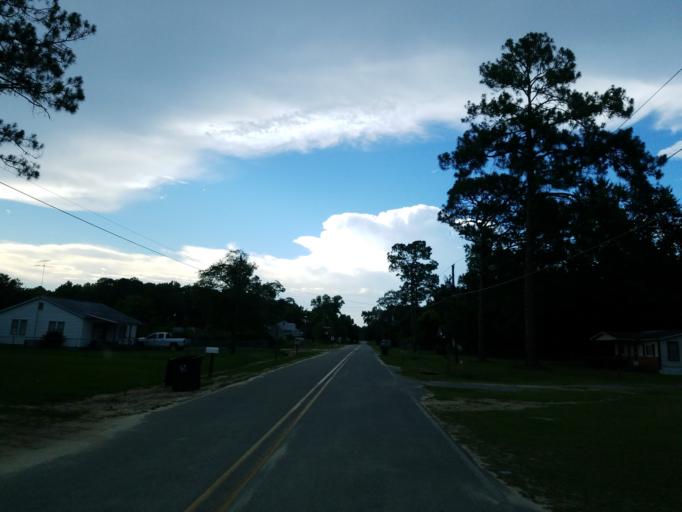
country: US
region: Georgia
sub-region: Cook County
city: Sparks
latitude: 31.2761
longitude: -83.4619
